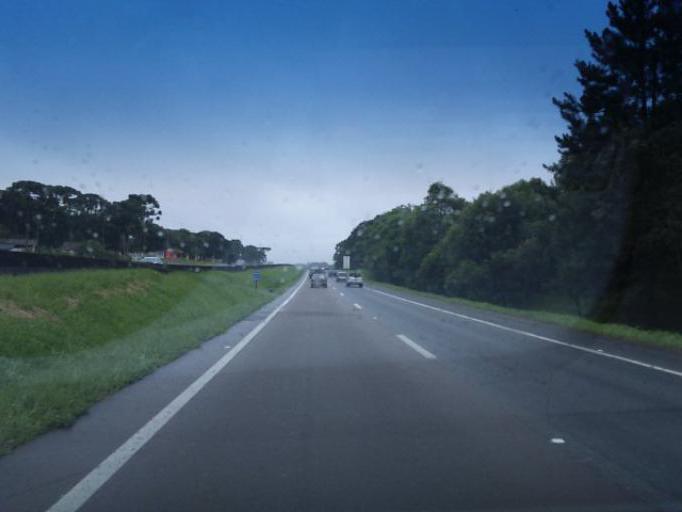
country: BR
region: Parana
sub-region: Sao Jose Dos Pinhais
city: Sao Jose dos Pinhais
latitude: -25.6508
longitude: -49.1575
